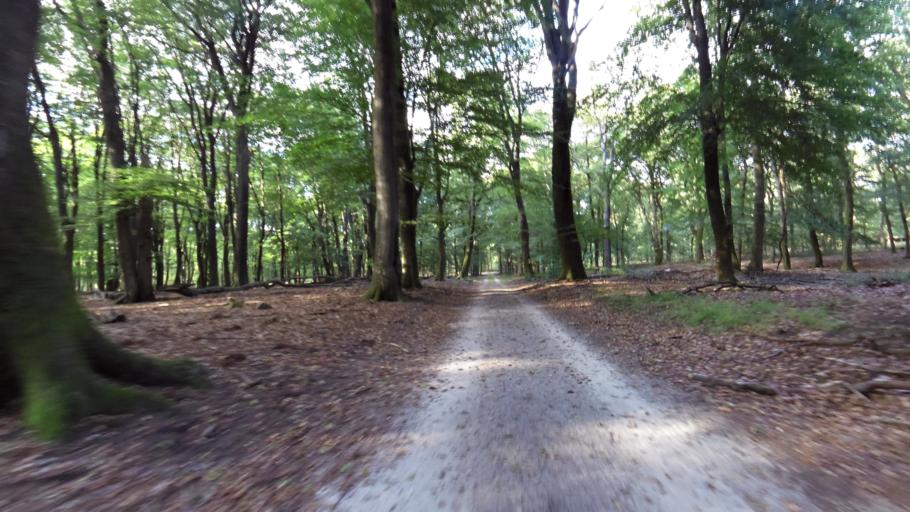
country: NL
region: Gelderland
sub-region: Gemeente Apeldoorn
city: Uddel
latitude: 52.2614
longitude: 5.8106
